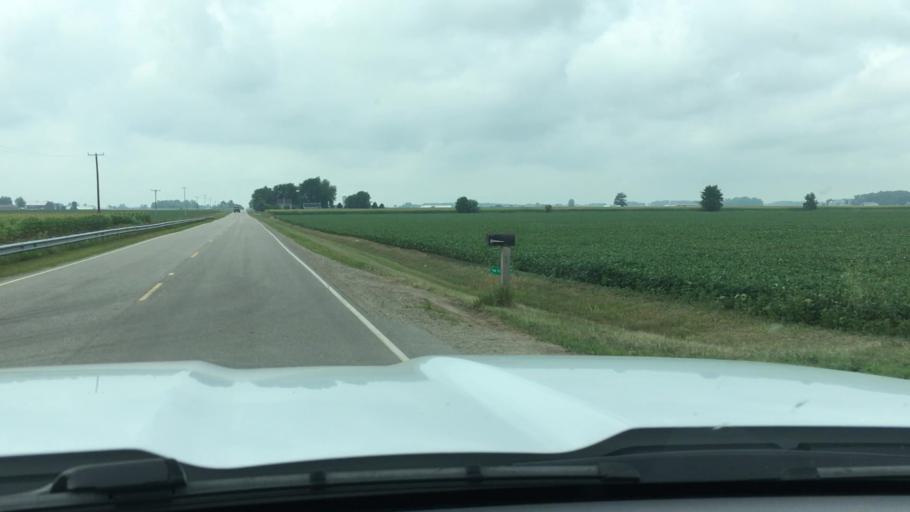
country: US
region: Michigan
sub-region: Sanilac County
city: Marlette
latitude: 43.3590
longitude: -82.9882
